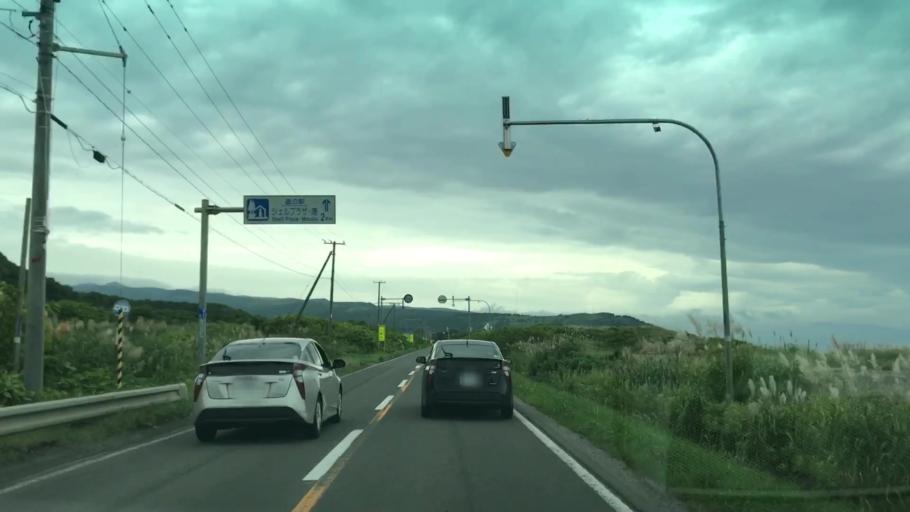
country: JP
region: Hokkaido
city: Iwanai
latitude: 42.8953
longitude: 140.3774
